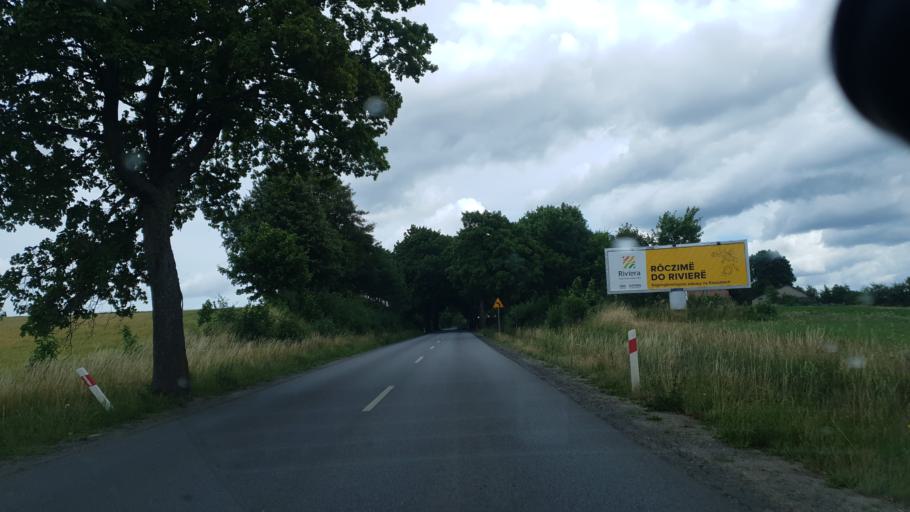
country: PL
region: Pomeranian Voivodeship
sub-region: Powiat kartuski
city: Zukowo
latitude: 54.3845
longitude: 18.3442
